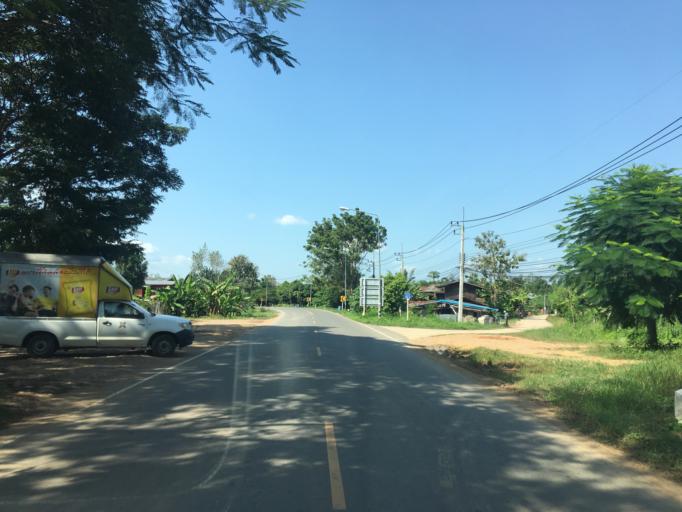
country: TH
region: Phayao
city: Chiang Muan
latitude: 18.8792
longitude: 100.2850
